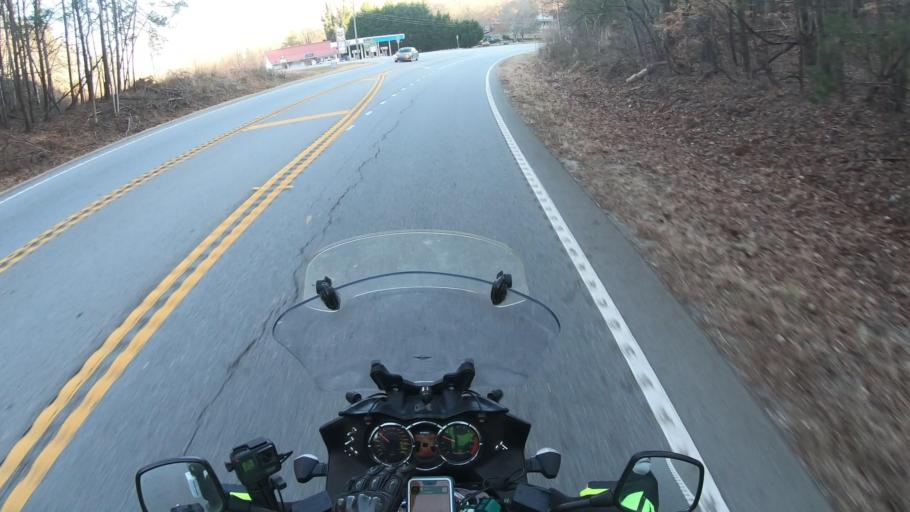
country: US
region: Georgia
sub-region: Lumpkin County
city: Dahlonega
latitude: 34.5638
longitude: -83.9688
